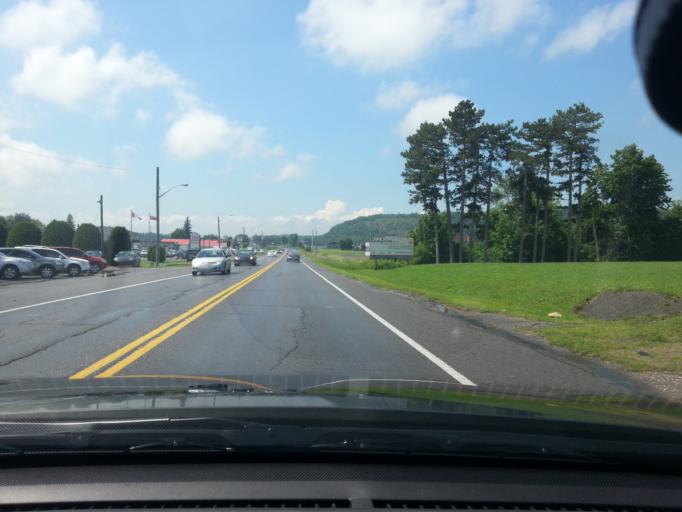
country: CA
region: Ontario
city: Renfrew
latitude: 45.4802
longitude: -76.6993
